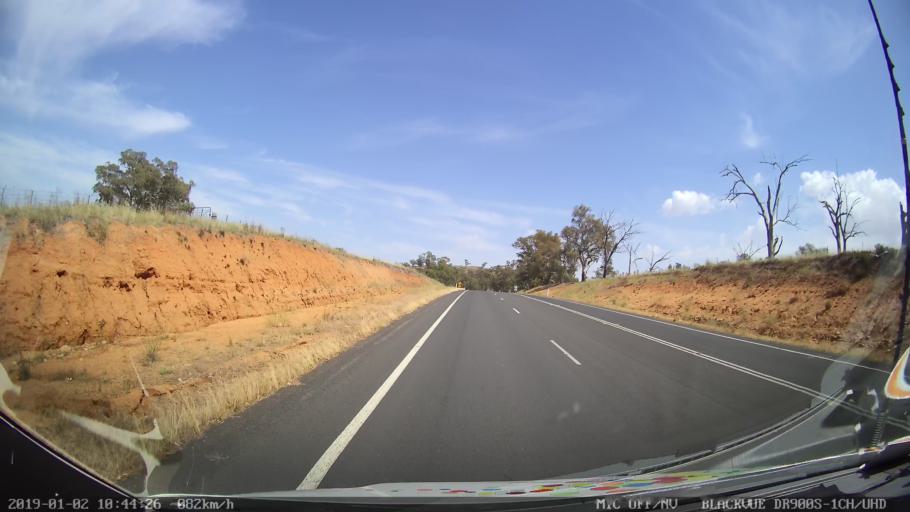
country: AU
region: New South Wales
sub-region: Cootamundra
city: Cootamundra
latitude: -34.7609
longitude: 148.2958
